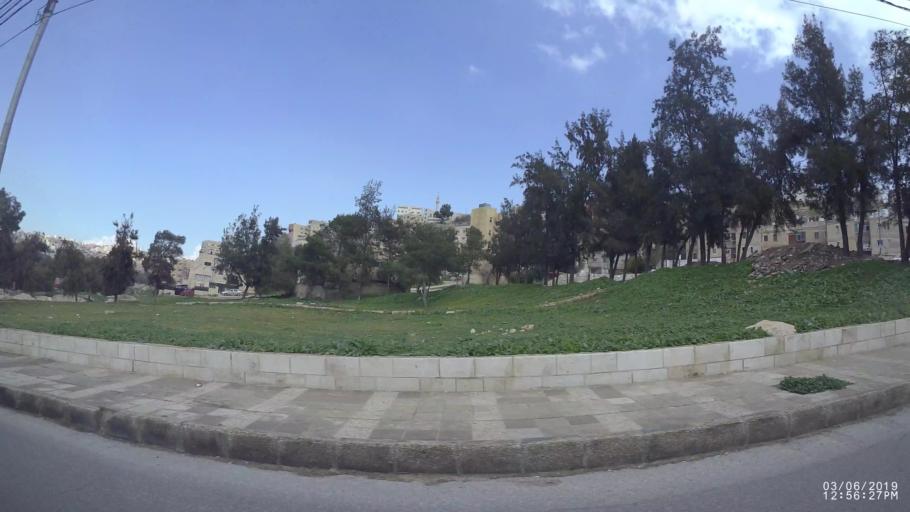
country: JO
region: Amman
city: Amman
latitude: 31.9808
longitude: 35.9772
